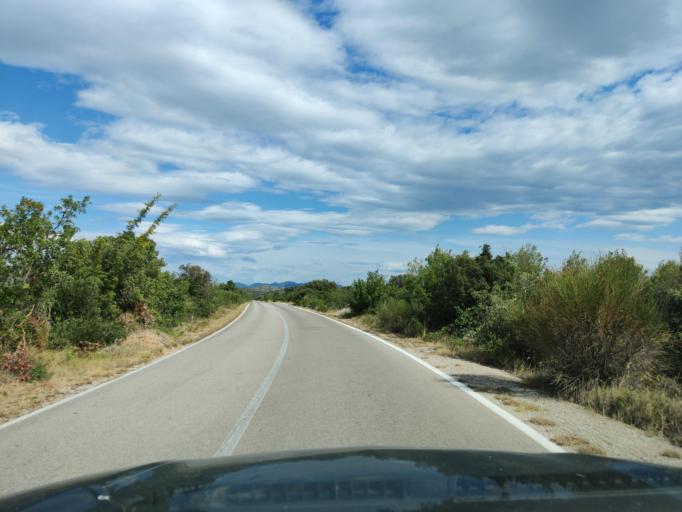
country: HR
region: Sibensko-Kniniska
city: Zaton
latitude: 43.7454
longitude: 15.8468
